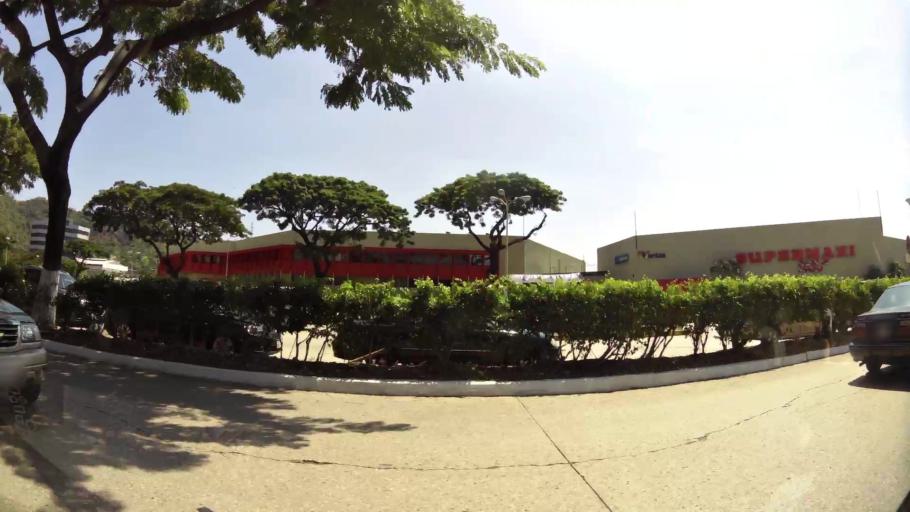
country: EC
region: Guayas
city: Guayaquil
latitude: -2.1695
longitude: -79.9157
